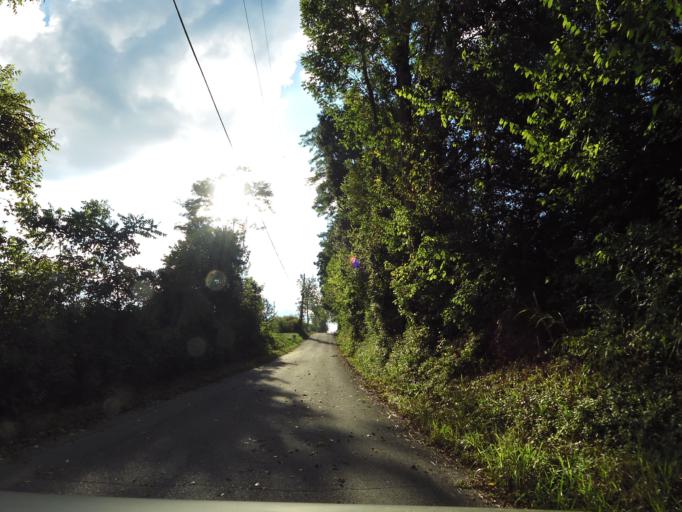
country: US
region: Tennessee
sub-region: Grainger County
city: Blaine
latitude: 36.1443
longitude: -83.7381
